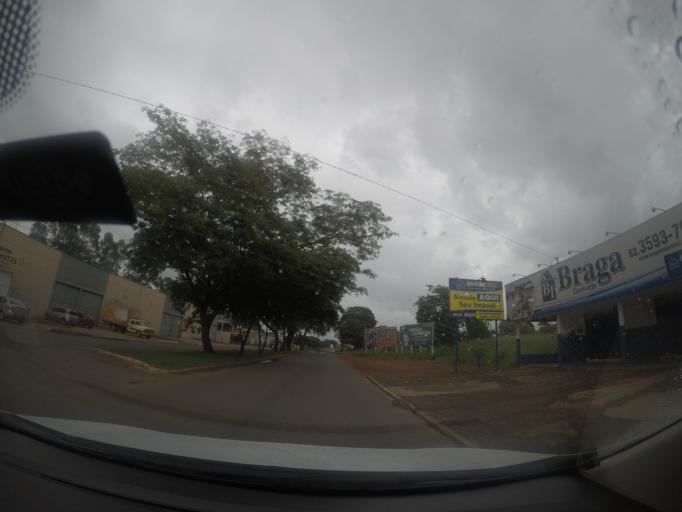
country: BR
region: Goias
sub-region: Trindade
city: Trindade
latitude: -16.6502
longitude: -49.3867
